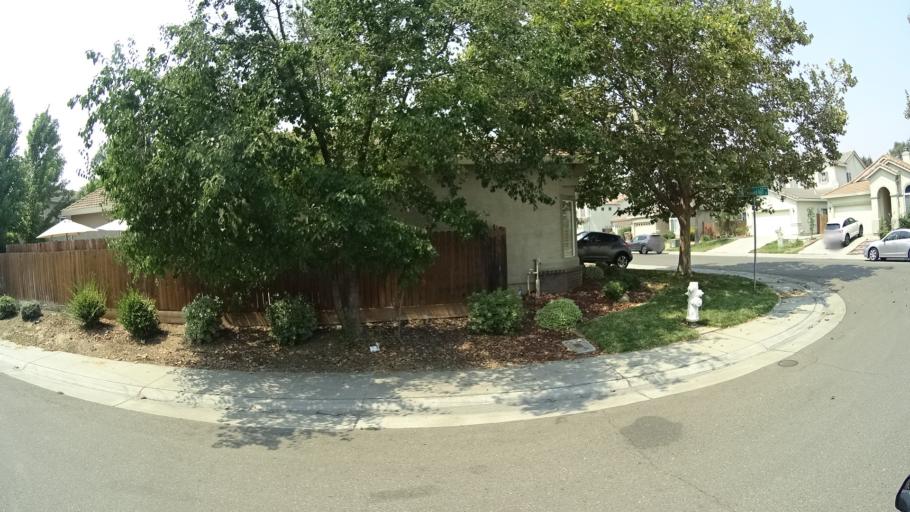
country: US
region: California
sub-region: Sacramento County
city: Laguna
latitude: 38.4080
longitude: -121.4347
